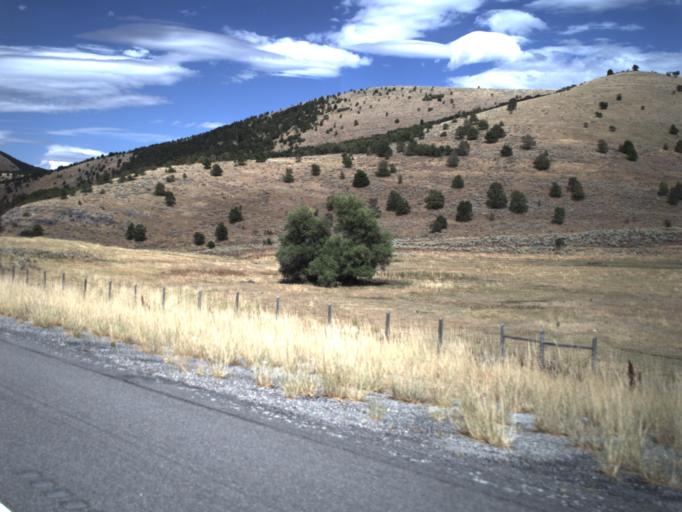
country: US
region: Utah
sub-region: Cache County
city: Wellsville
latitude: 41.5861
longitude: -111.9757
